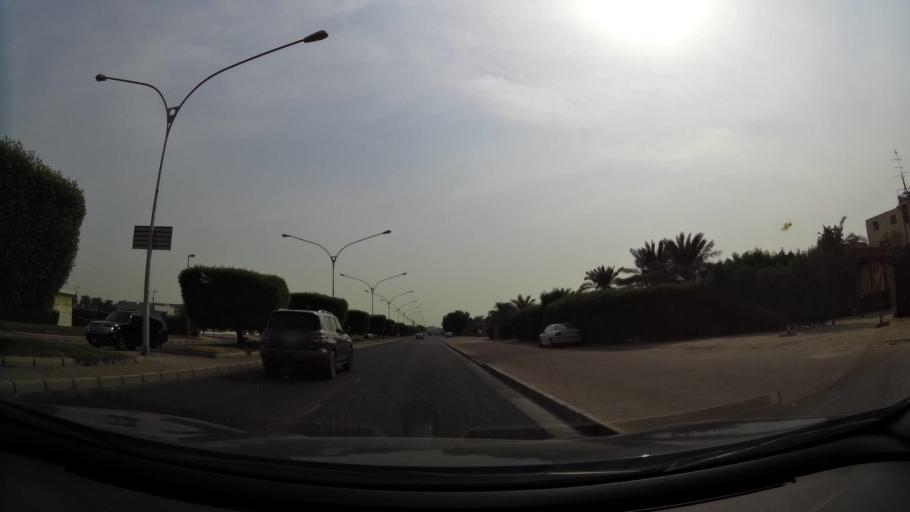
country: KW
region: Al Asimah
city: Ar Rabiyah
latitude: 29.2941
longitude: 47.9390
